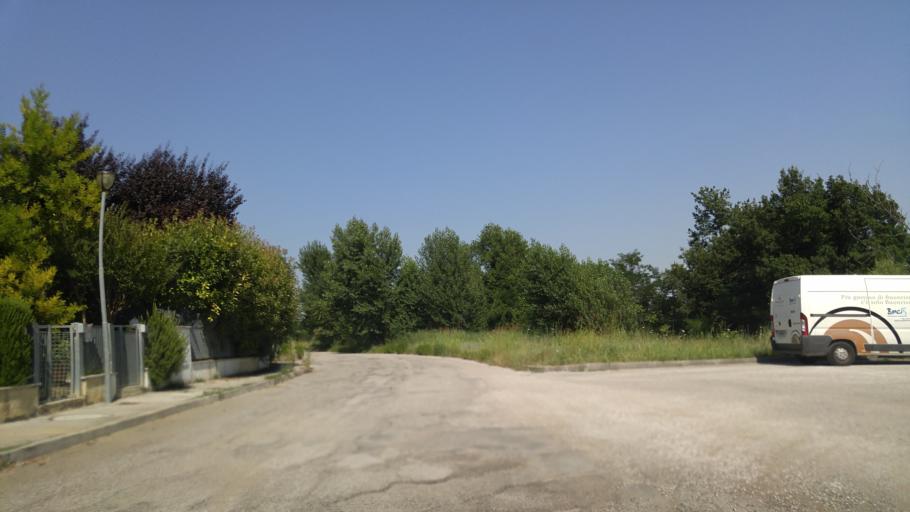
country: IT
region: The Marches
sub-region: Provincia di Pesaro e Urbino
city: Fossombrone
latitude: 43.6933
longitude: 12.8258
